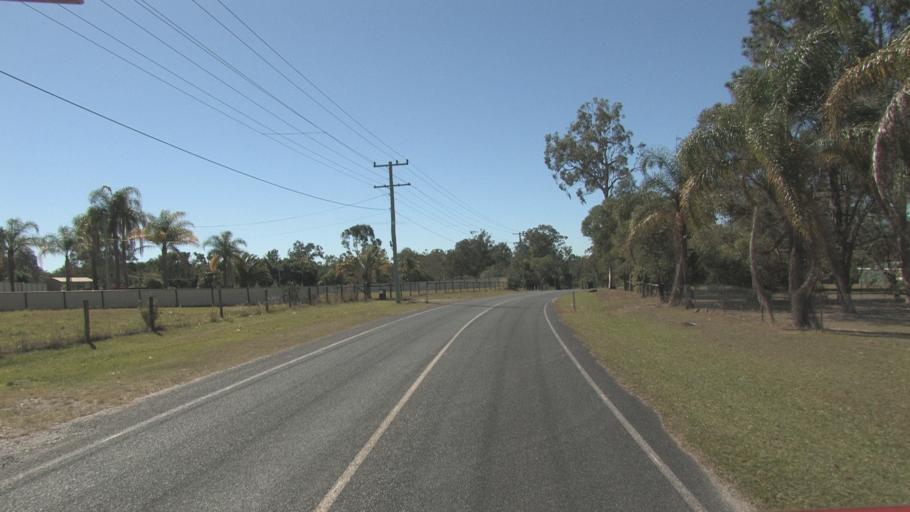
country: AU
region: Queensland
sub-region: Logan
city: Park Ridge South
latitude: -27.7245
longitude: 153.0537
